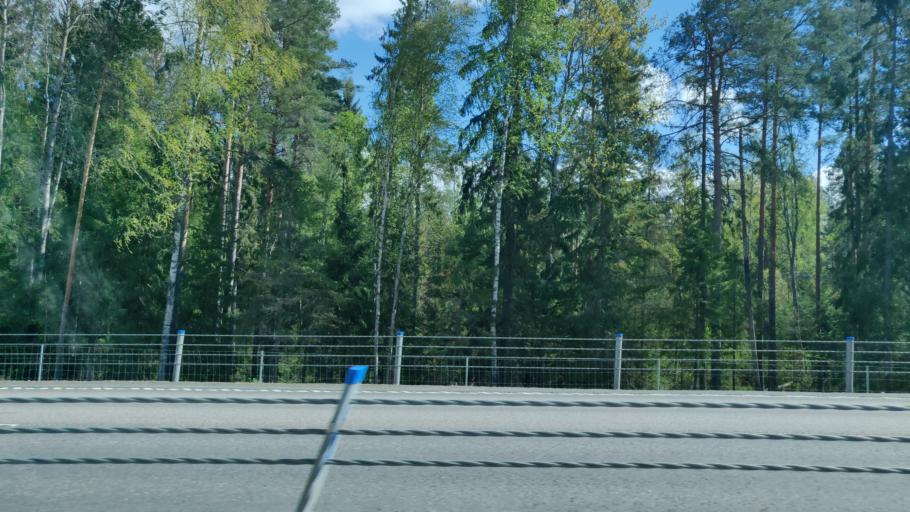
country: SE
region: Vaermland
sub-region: Karlstads Kommun
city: Karlstad
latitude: 59.4301
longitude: 13.5377
